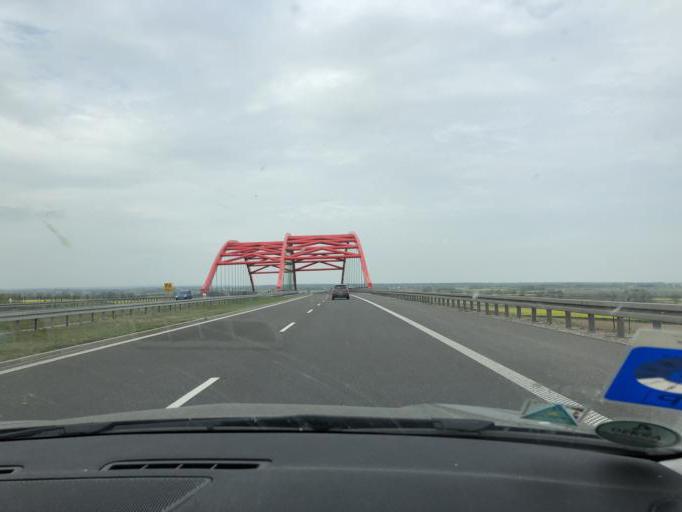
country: PL
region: Subcarpathian Voivodeship
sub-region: Powiat przeworski
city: Rozborz
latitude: 50.0618
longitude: 22.5660
